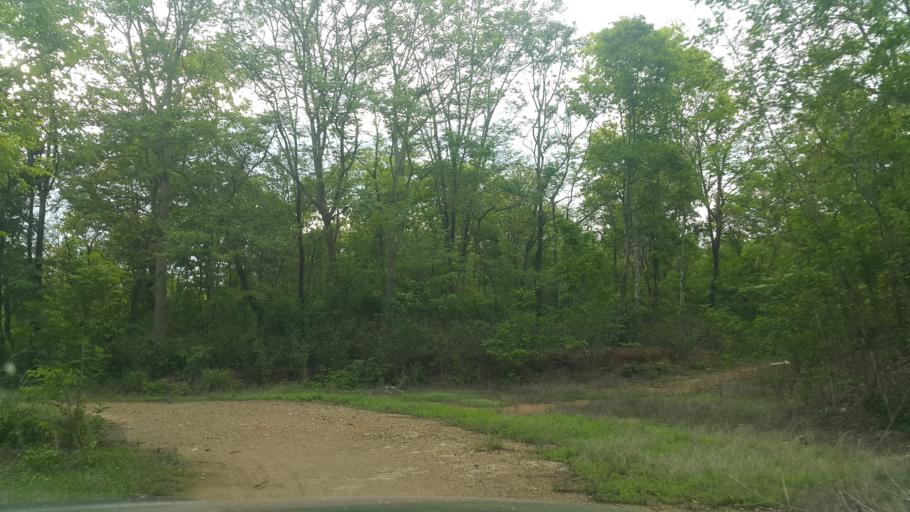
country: TH
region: Chiang Mai
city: Mae On
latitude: 18.7196
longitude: 99.2198
